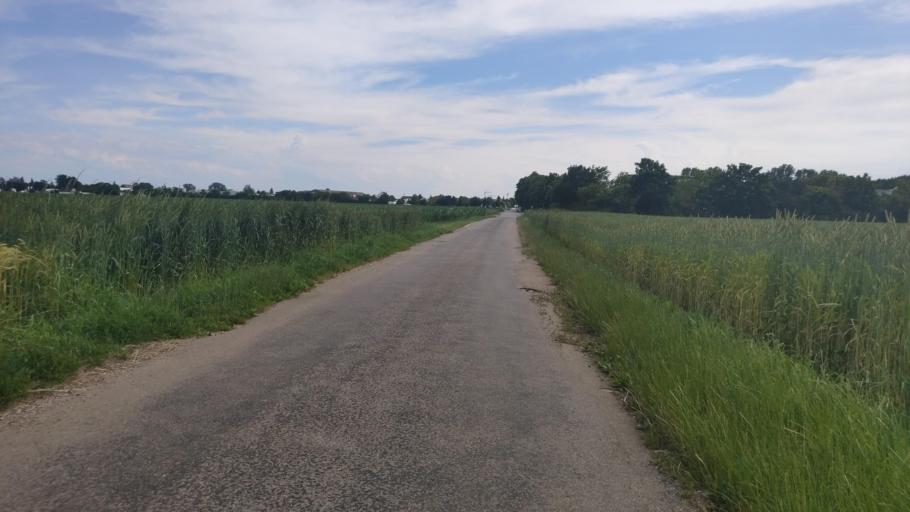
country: DE
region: Bavaria
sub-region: Swabia
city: Konigsbrunn
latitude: 48.2606
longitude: 10.8755
